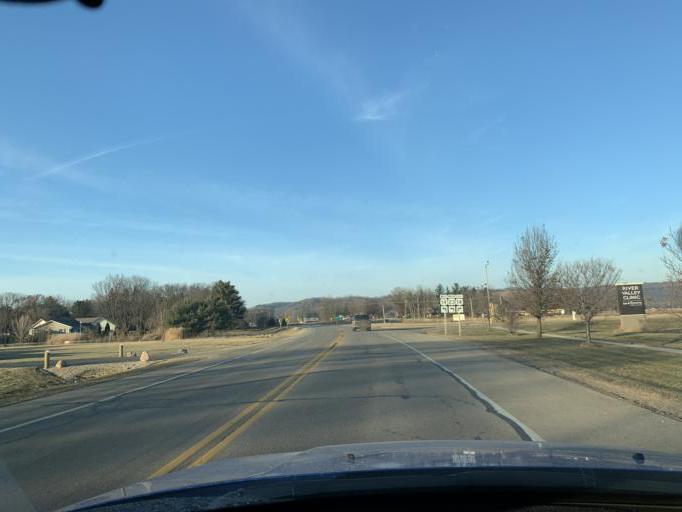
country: US
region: Wisconsin
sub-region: Sauk County
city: Spring Green
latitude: 43.1828
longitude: -90.0640
